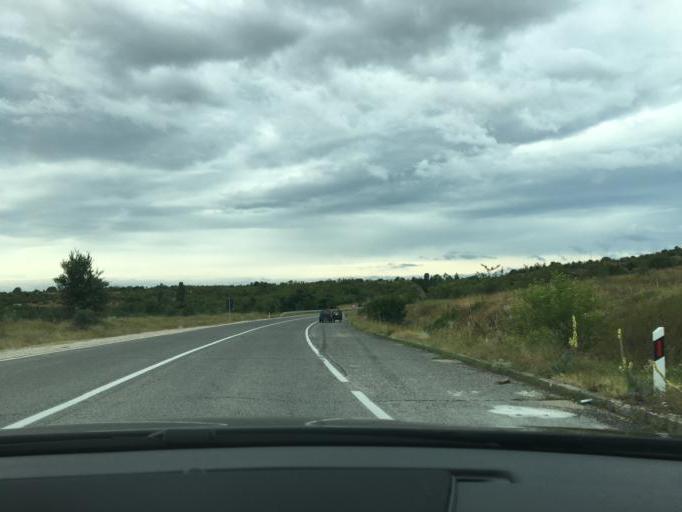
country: MK
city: Klechovce
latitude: 42.1523
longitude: 21.9535
